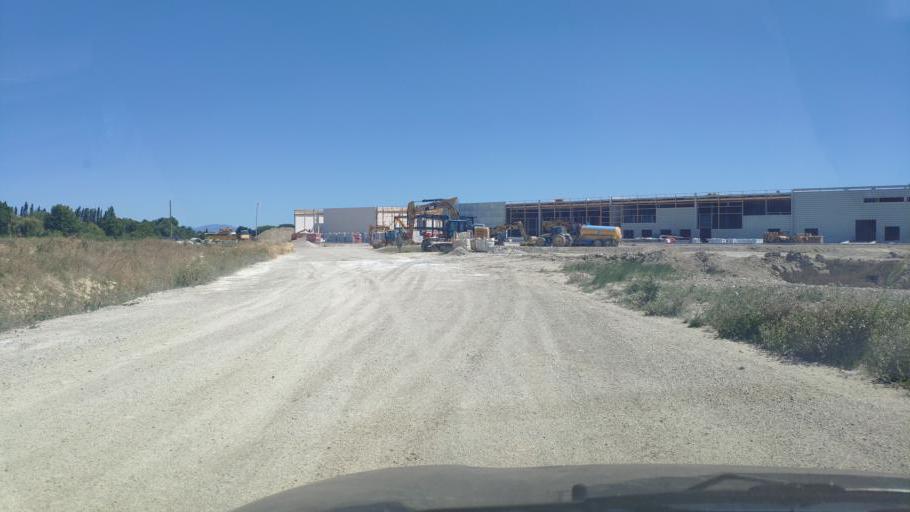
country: FR
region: Provence-Alpes-Cote d'Azur
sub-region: Departement du Vaucluse
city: Jonquieres
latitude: 44.1064
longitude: 4.8877
